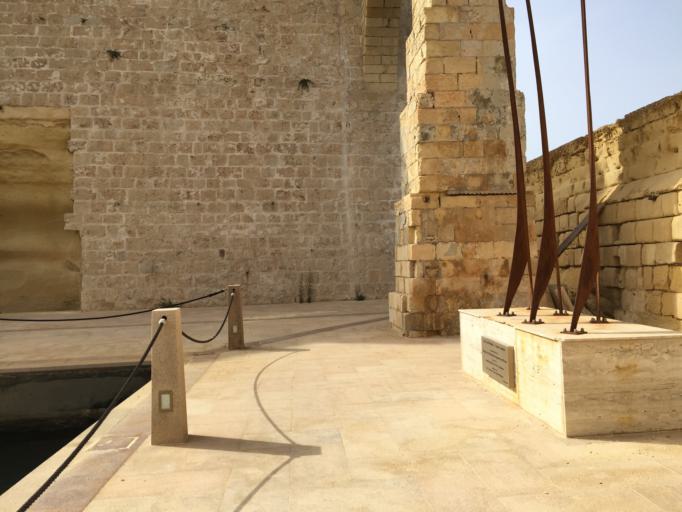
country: MT
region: Il-Birgu
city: Vittoriosa
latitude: 35.8911
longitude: 14.5198
